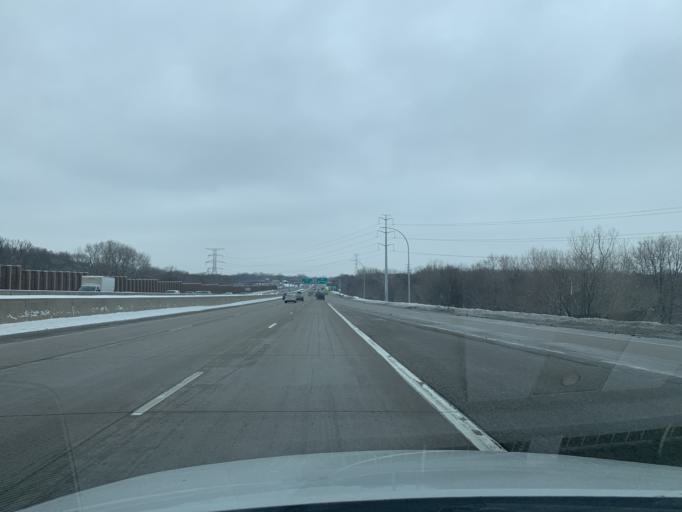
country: US
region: Minnesota
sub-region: Anoka County
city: Coon Rapids
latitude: 45.1352
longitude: -93.2944
